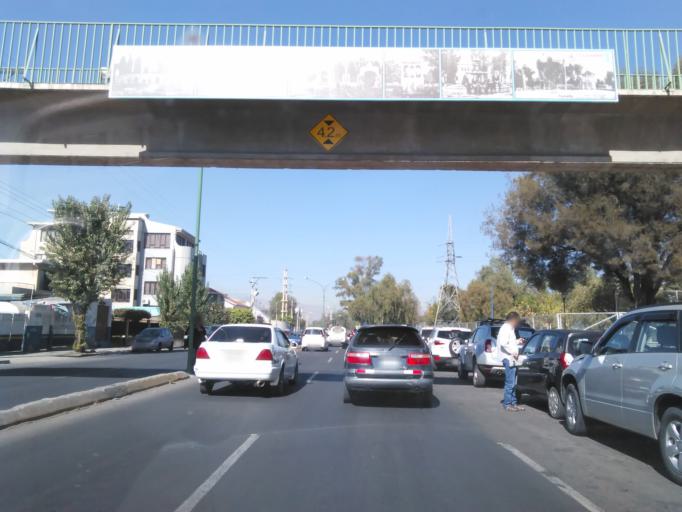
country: BO
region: Cochabamba
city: Cochabamba
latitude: -17.3914
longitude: -66.1654
